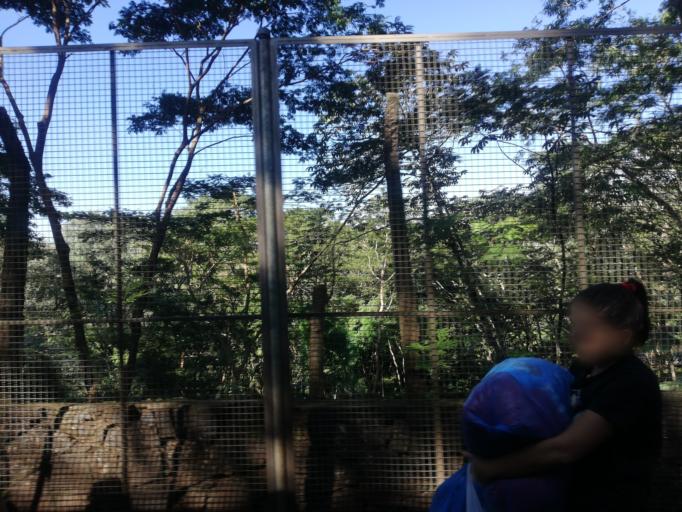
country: PY
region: Alto Parana
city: Ciudad del Este
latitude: -25.5096
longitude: -54.6045
